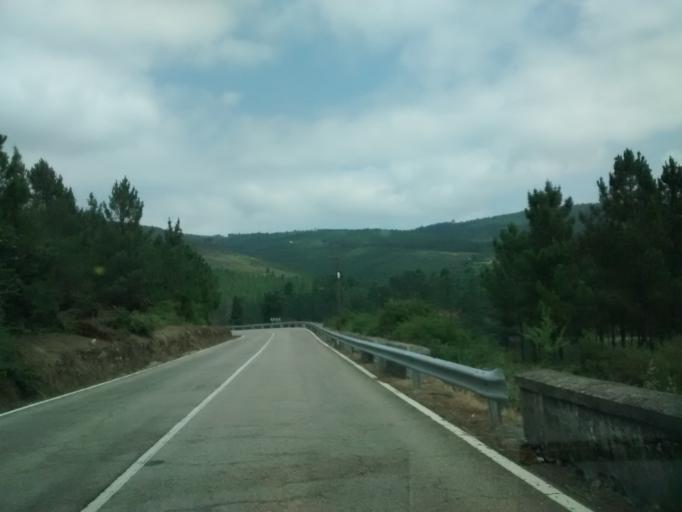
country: ES
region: Galicia
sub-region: Provincia de Ourense
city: Petin
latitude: 42.3405
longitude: -7.1767
